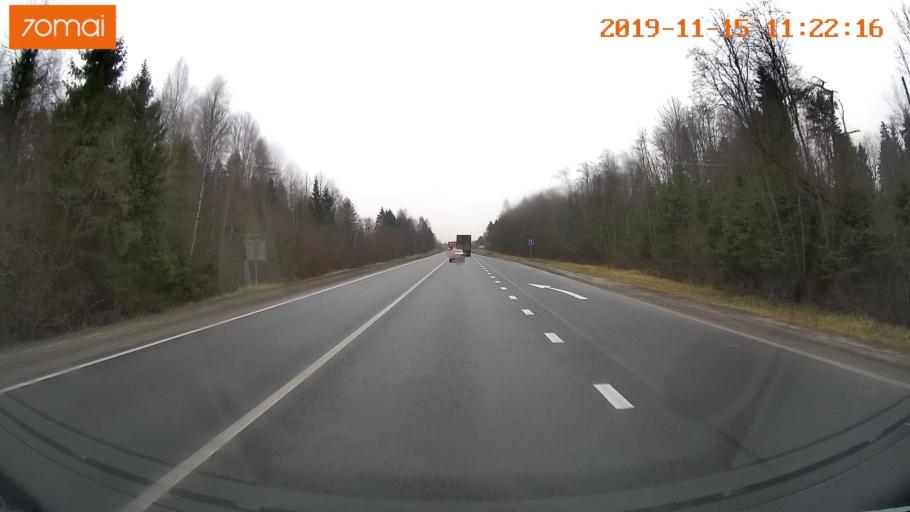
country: RU
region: Vologda
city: Molochnoye
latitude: 59.1472
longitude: 39.3584
